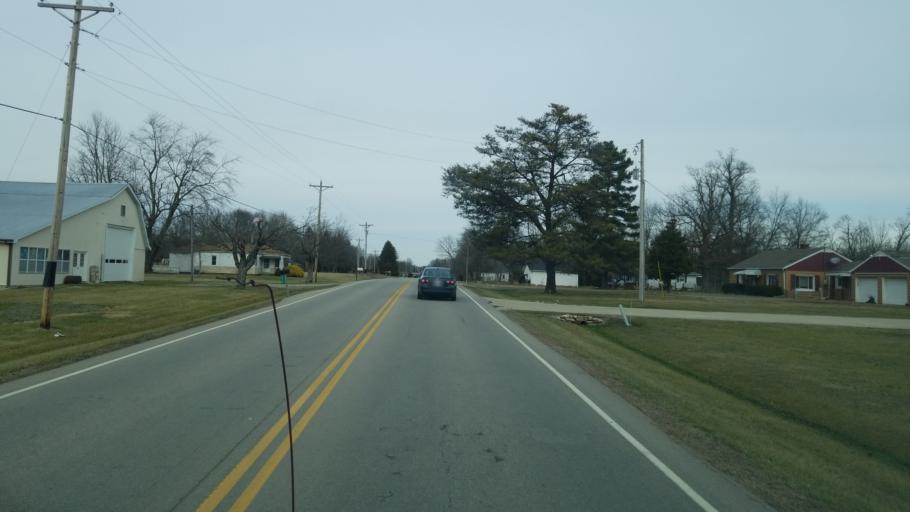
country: US
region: Ohio
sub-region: Adams County
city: Winchester
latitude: 39.0774
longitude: -83.6858
